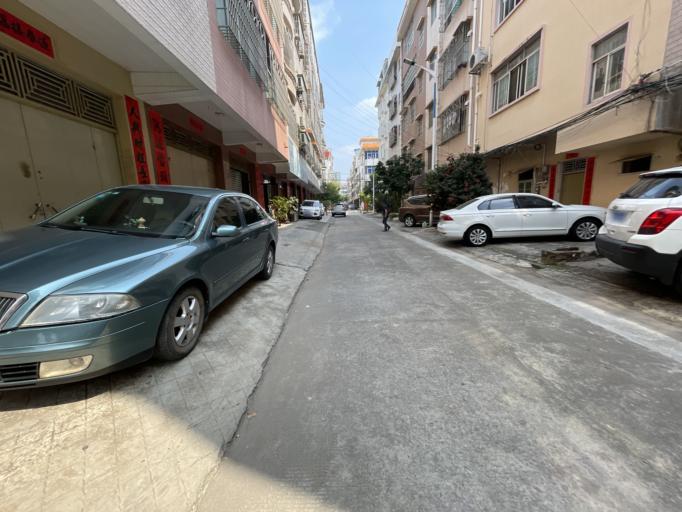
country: CN
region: Guangxi Zhuangzu Zizhiqu
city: Qinzhou
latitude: 21.9695
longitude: 108.6282
